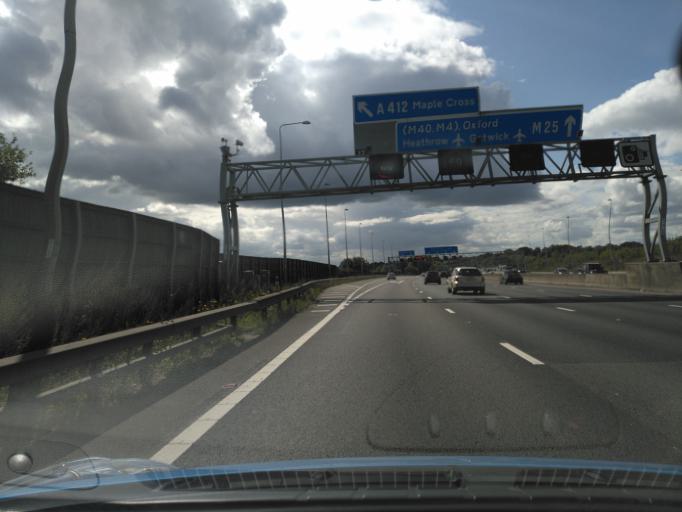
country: GB
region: England
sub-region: Hertfordshire
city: Chorleywood
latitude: 51.6420
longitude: -0.5031
